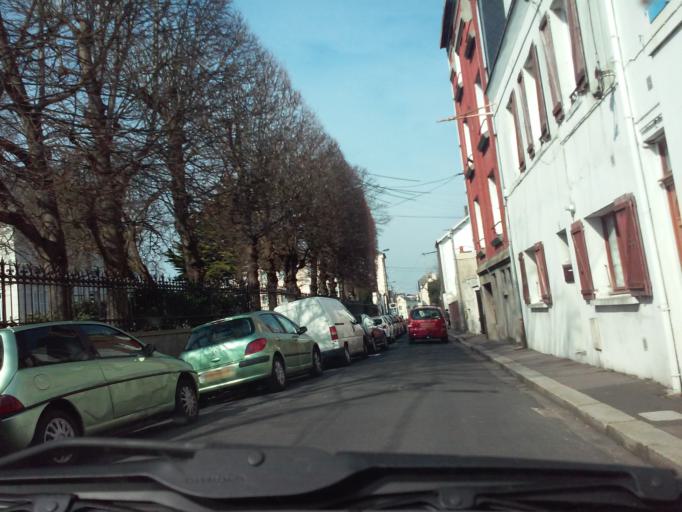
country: FR
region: Haute-Normandie
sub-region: Departement de la Seine-Maritime
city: Le Havre
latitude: 49.5070
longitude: 0.1076
